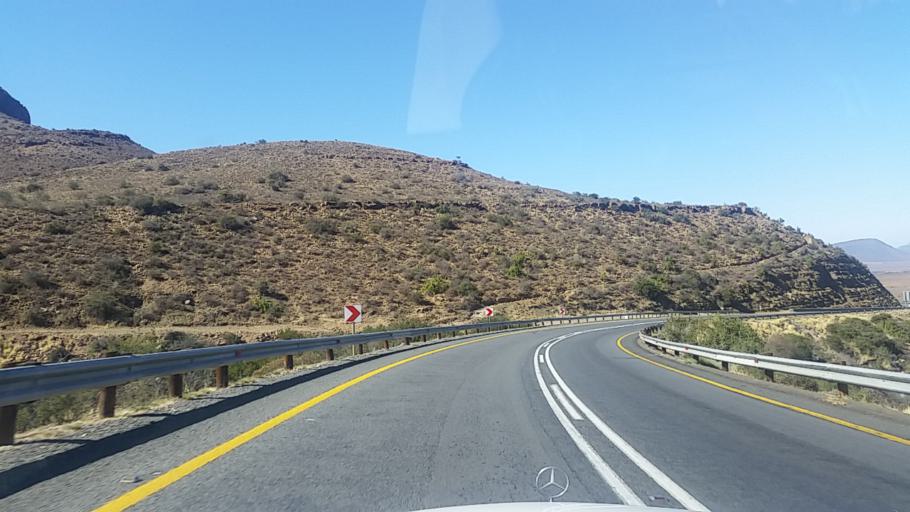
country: ZA
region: Eastern Cape
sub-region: Cacadu District Municipality
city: Graaff-Reinet
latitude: -32.1114
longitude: 24.6097
